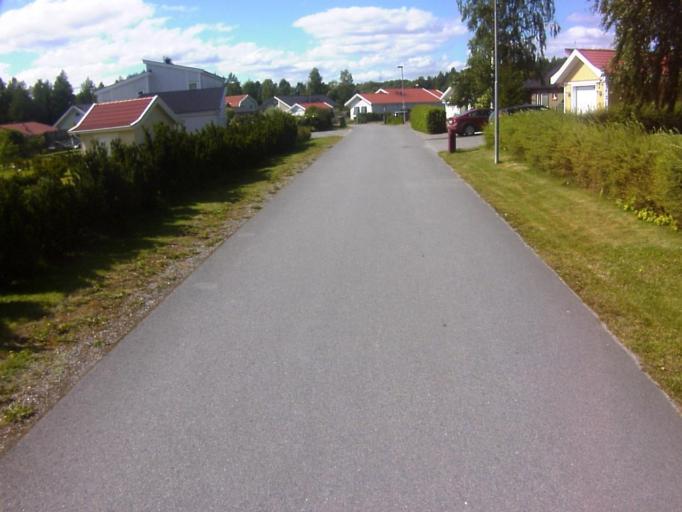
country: SE
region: Soedermanland
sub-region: Eskilstuna Kommun
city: Hallbybrunn
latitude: 59.3428
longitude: 16.4254
